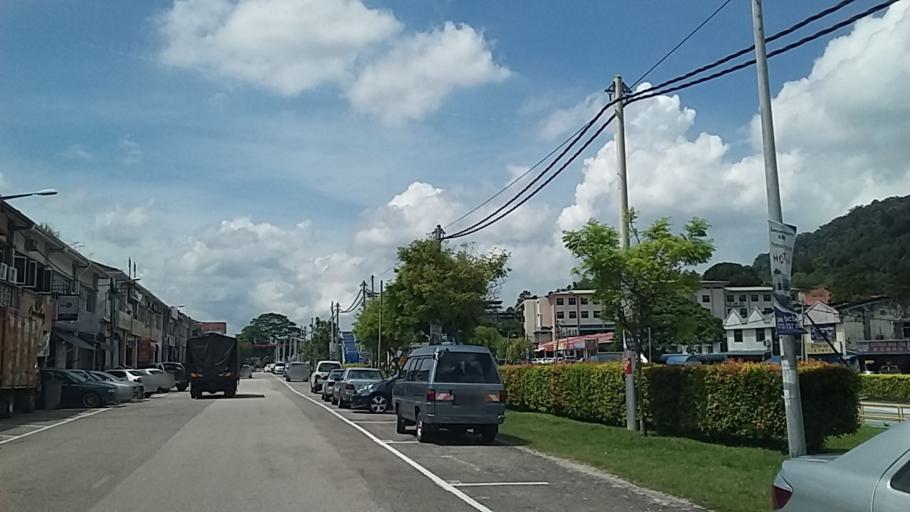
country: MY
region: Johor
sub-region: Daerah Batu Pahat
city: Batu Pahat
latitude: 1.8370
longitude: 102.9474
